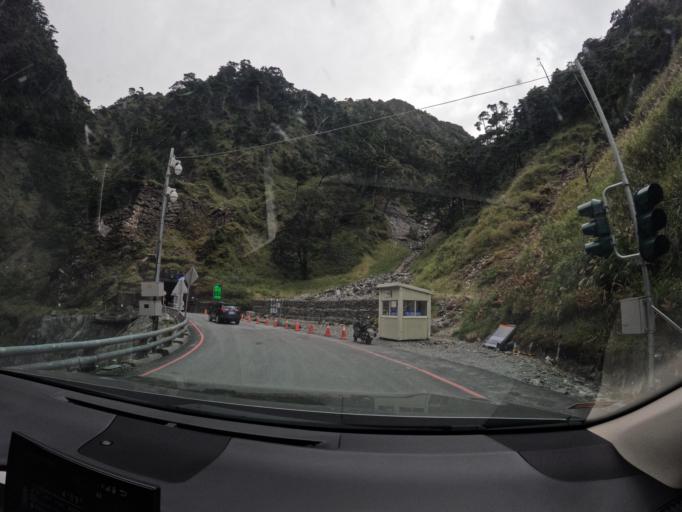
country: TW
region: Taiwan
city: Yujing
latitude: 23.2659
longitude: 120.9549
